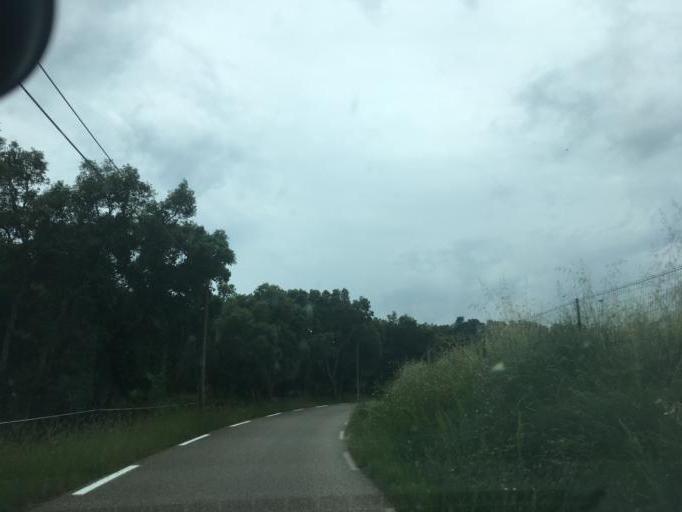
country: FR
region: Provence-Alpes-Cote d'Azur
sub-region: Departement du Var
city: La Londe-les-Maures
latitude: 43.1813
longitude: 6.2147
